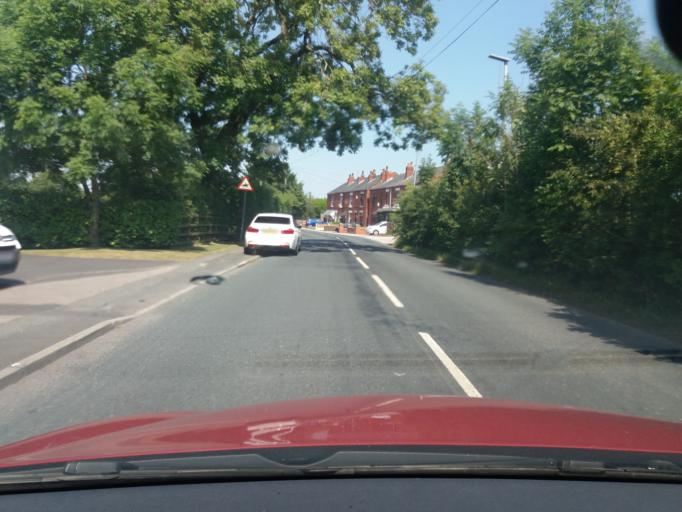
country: GB
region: England
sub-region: Lancashire
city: Coppull
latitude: 53.6295
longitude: -2.6732
